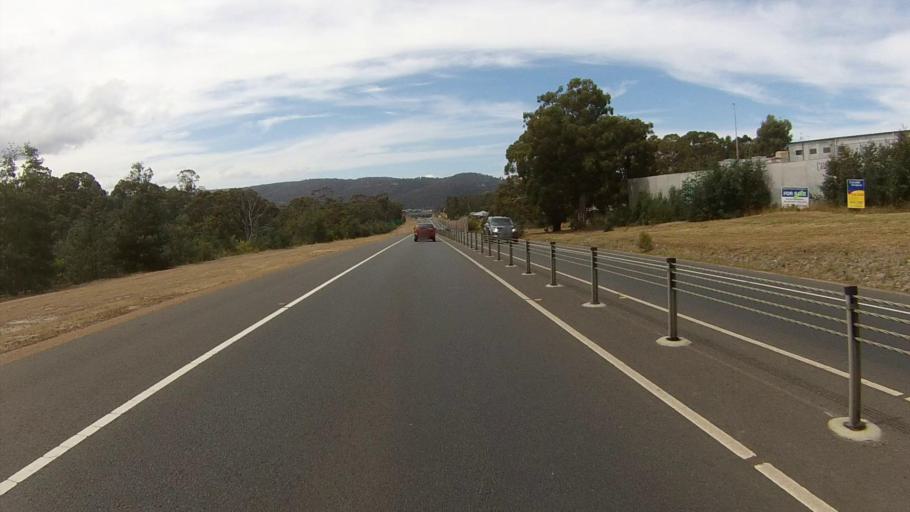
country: AU
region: Tasmania
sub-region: Kingborough
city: Kingston
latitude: -42.9806
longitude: 147.2932
